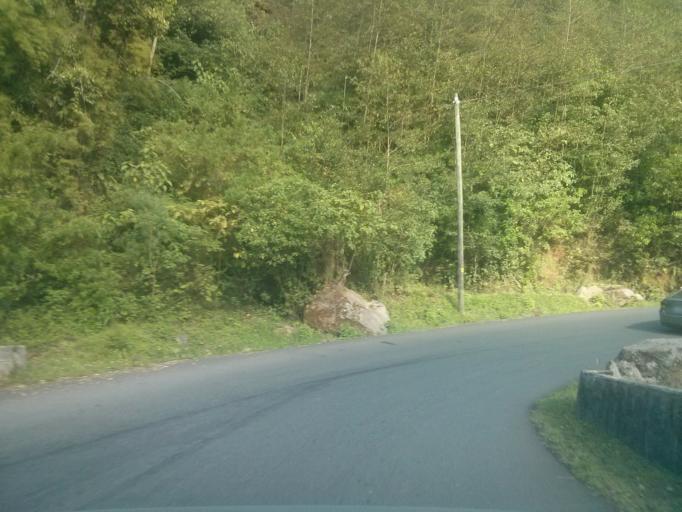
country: CR
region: Heredia
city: Santo Domingo
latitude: 10.1342
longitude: -84.1601
